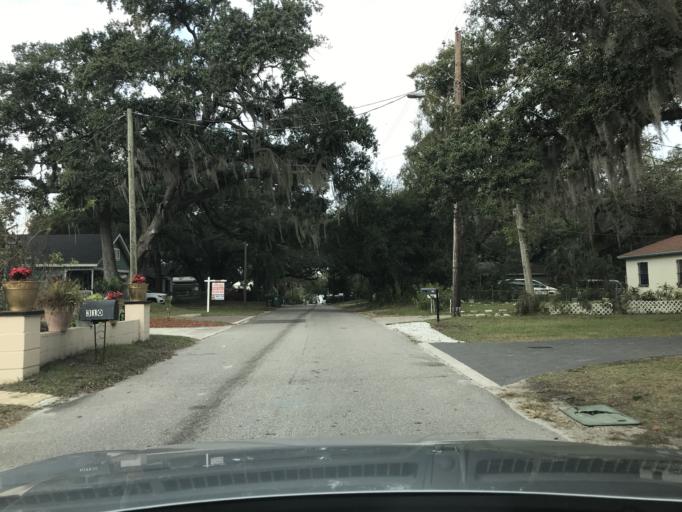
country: US
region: Florida
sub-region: Hillsborough County
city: Egypt Lake-Leto
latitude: 27.9977
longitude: -82.4643
